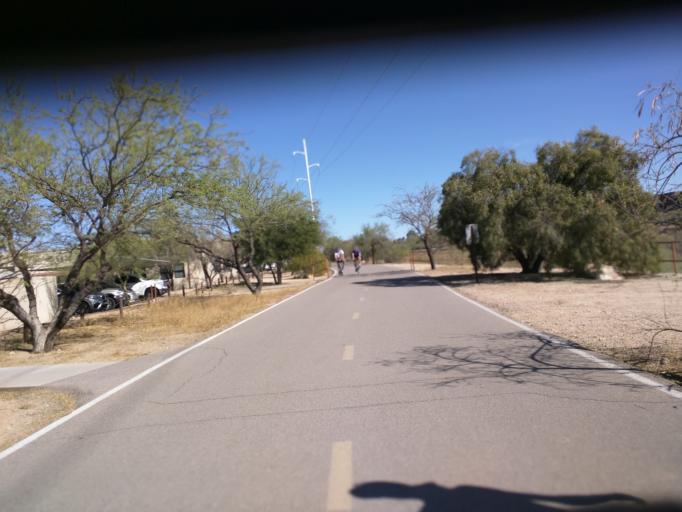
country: US
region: Arizona
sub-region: Pima County
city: Catalina Foothills
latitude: 32.2891
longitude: -110.9593
